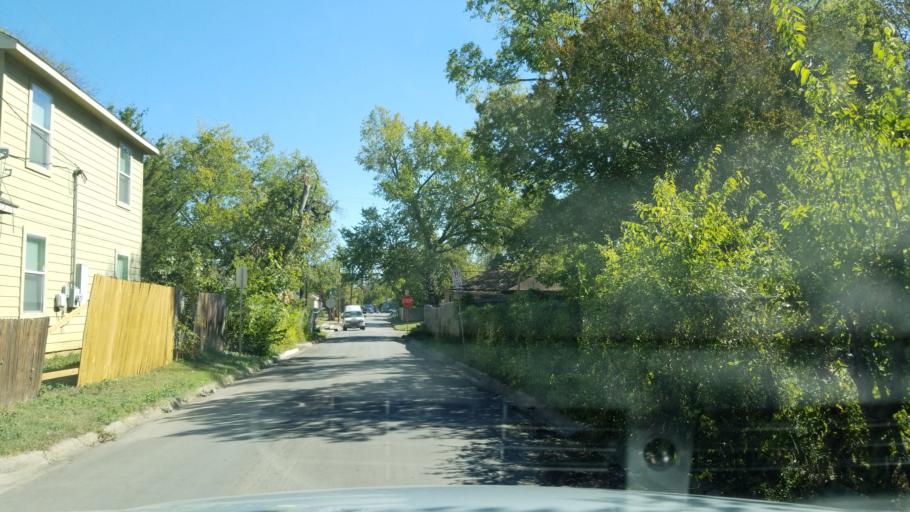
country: US
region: Texas
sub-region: Dallas County
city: Dallas
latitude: 32.7779
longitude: -96.7440
